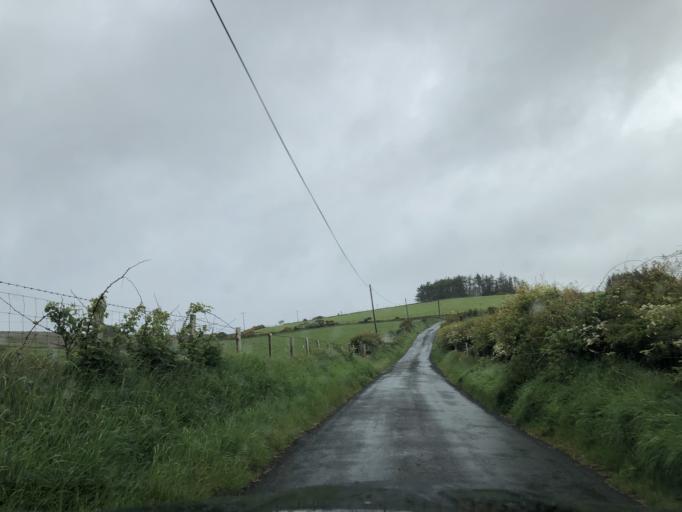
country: GB
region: Northern Ireland
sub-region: Moyle District
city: Ballycastle
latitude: 55.2043
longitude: -6.1721
